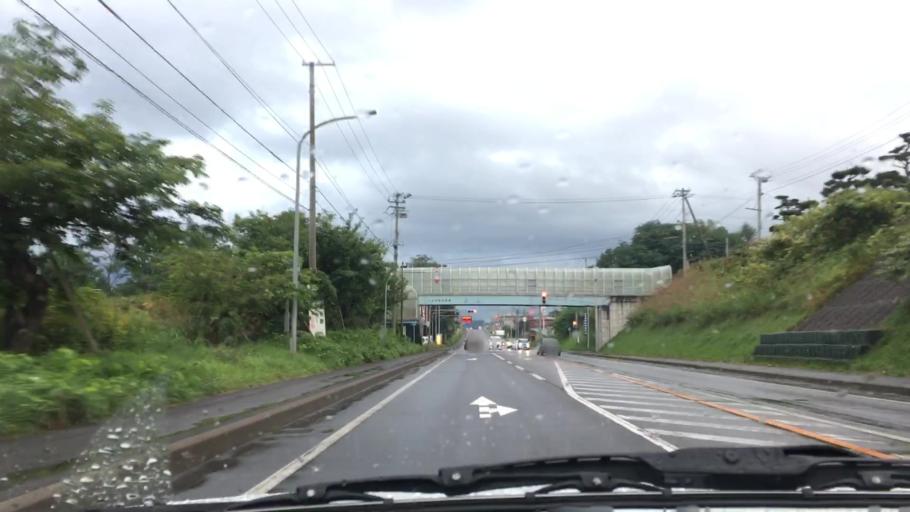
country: JP
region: Hokkaido
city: Nanae
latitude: 42.0975
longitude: 140.5700
